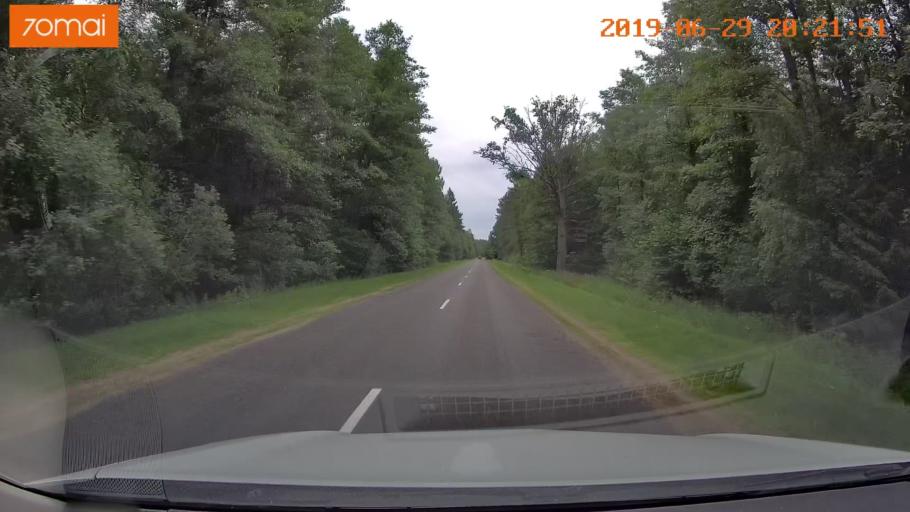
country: BY
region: Brest
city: Asnyezhytsy
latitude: 52.4246
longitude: 26.2533
